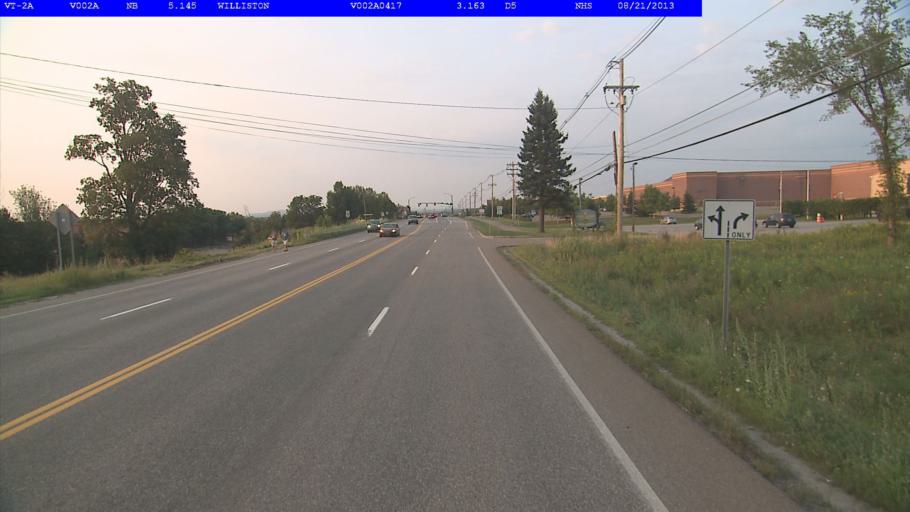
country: US
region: Vermont
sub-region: Chittenden County
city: Williston
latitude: 44.4418
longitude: -73.1136
